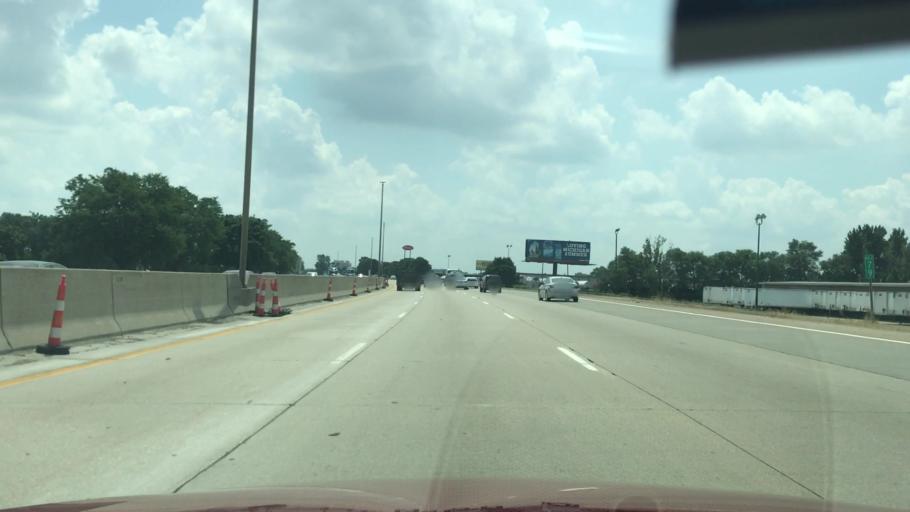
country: US
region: Michigan
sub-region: Kent County
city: Kentwood
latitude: 42.8806
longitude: -85.6818
